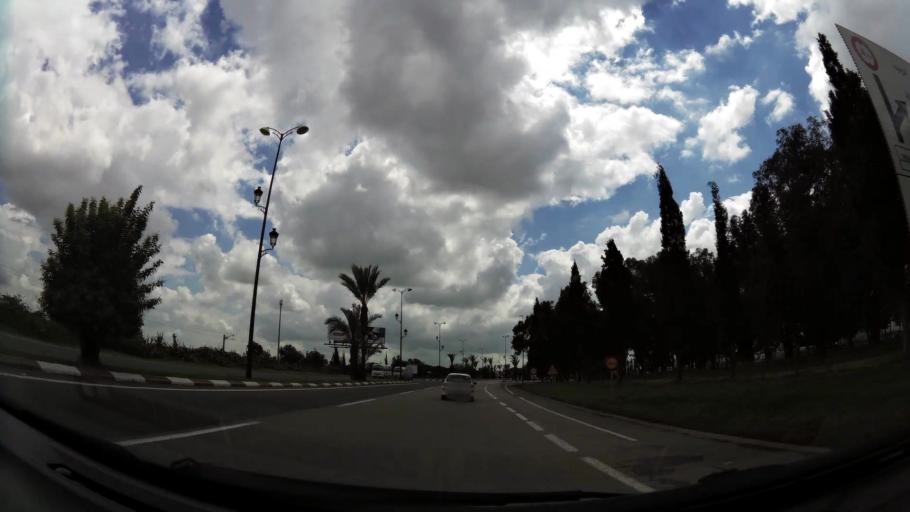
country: MA
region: Chaouia-Ouardigha
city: Nouaseur
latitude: 33.3833
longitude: -7.5649
